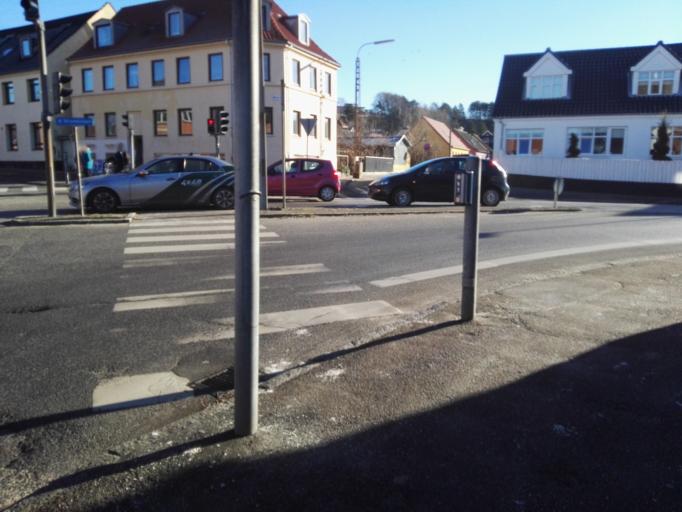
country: DK
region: Capital Region
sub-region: Halsnaes Kommune
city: Frederiksvaerk
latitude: 55.9696
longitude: 12.0204
